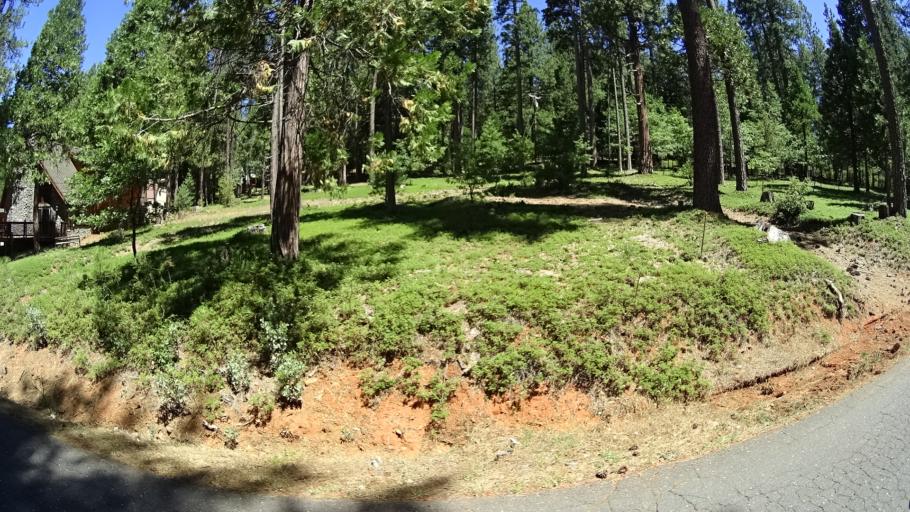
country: US
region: California
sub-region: Calaveras County
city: Arnold
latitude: 38.2362
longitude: -120.3371
